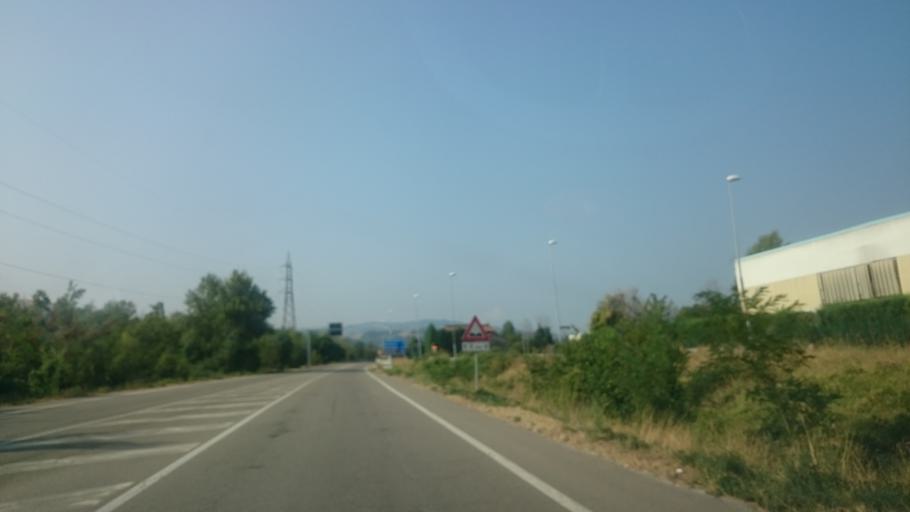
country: IT
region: Emilia-Romagna
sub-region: Provincia di Reggio Emilia
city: Castellarano
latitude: 44.5171
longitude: 10.7436
